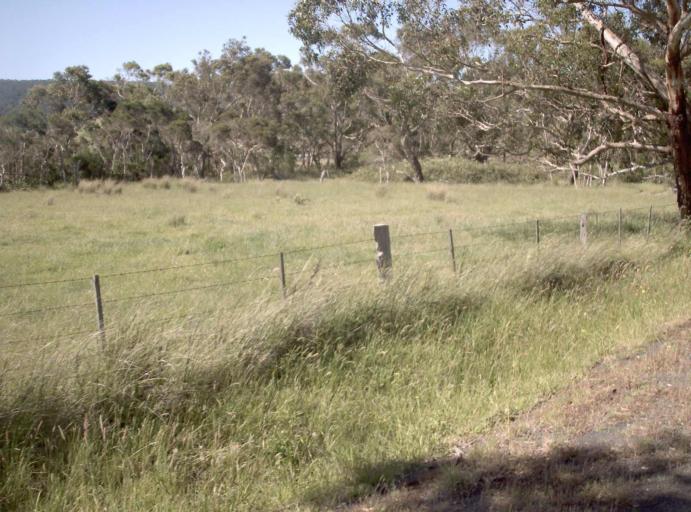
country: AU
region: Victoria
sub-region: Latrobe
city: Morwell
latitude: -38.6371
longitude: 146.5245
